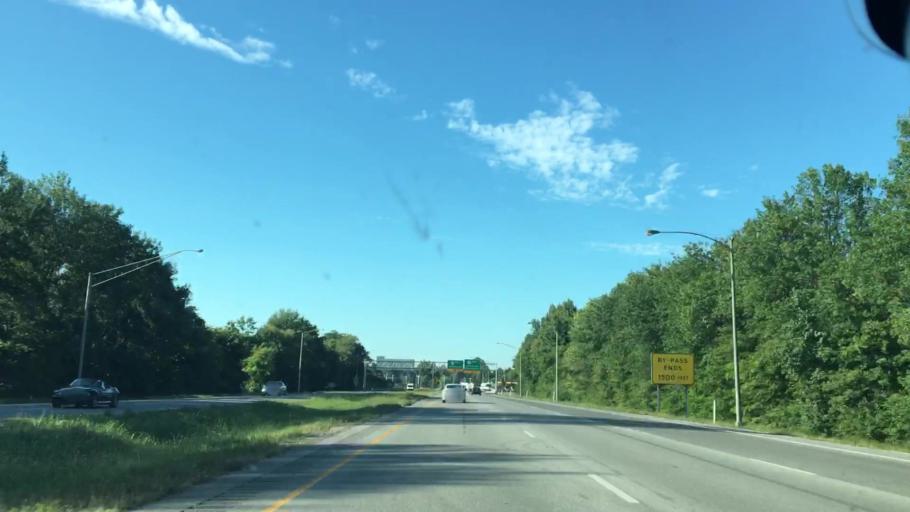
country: US
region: Kentucky
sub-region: Daviess County
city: Owensboro
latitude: 37.7705
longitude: -87.1649
